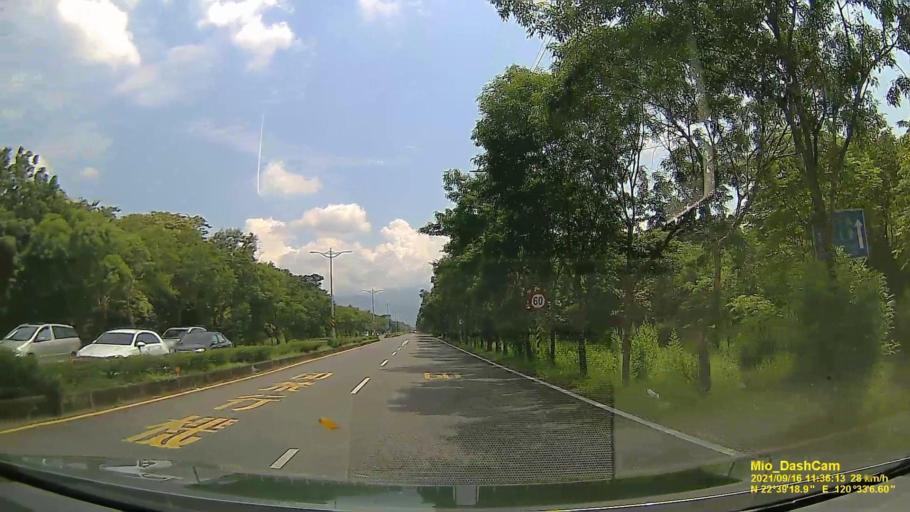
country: TW
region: Taiwan
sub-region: Pingtung
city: Pingtung
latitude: 22.6553
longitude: 120.5518
